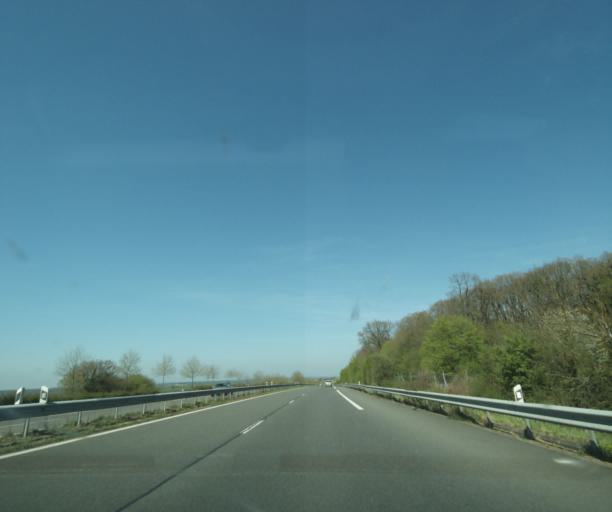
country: FR
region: Bourgogne
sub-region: Departement de la Nievre
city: Chaulgnes
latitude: 47.1189
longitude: 3.0578
